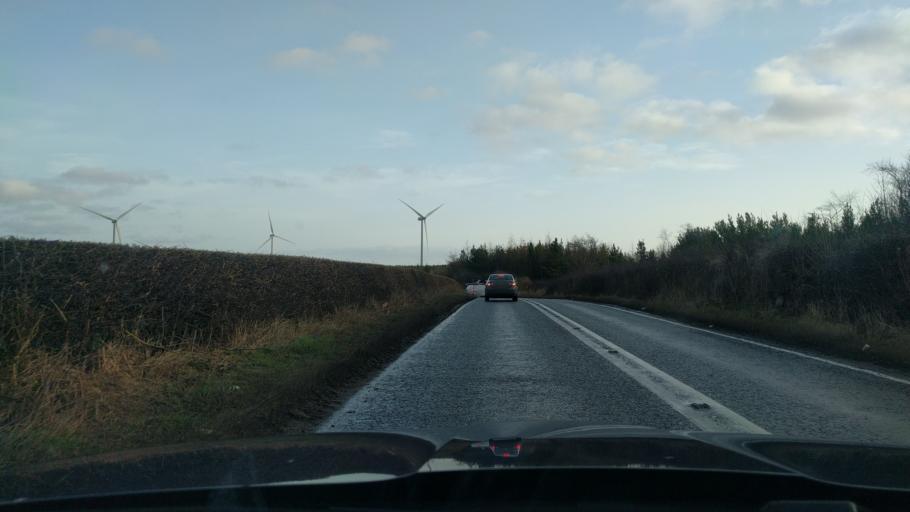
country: GB
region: England
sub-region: Northumberland
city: Ashington
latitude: 55.1992
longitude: -1.5824
